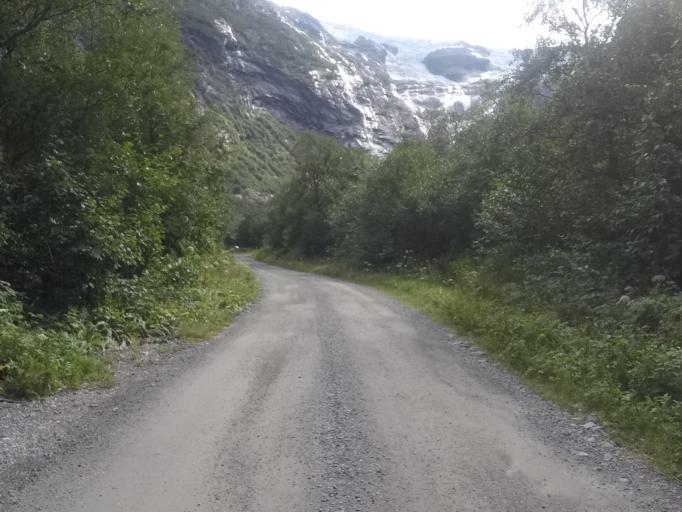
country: NO
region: Sogn og Fjordane
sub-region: Stryn
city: Stryn
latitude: 61.7483
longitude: 7.0347
